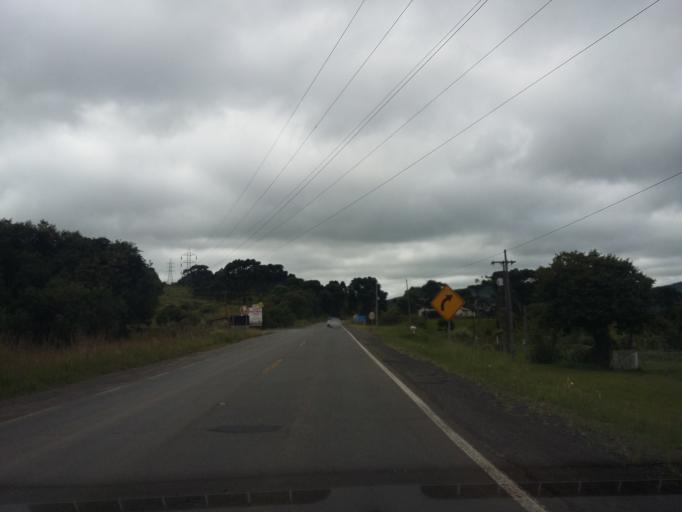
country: BR
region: Santa Catarina
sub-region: Lages
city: Lages
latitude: -27.8603
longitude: -50.2133
